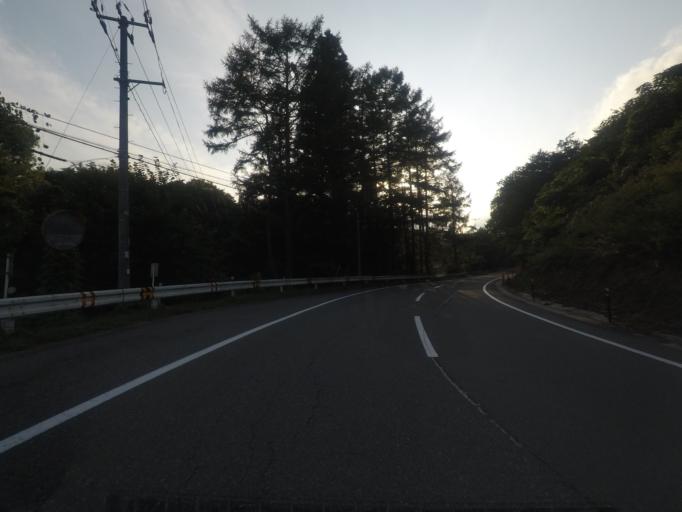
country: JP
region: Fukushima
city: Namie
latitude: 37.5548
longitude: 140.7823
